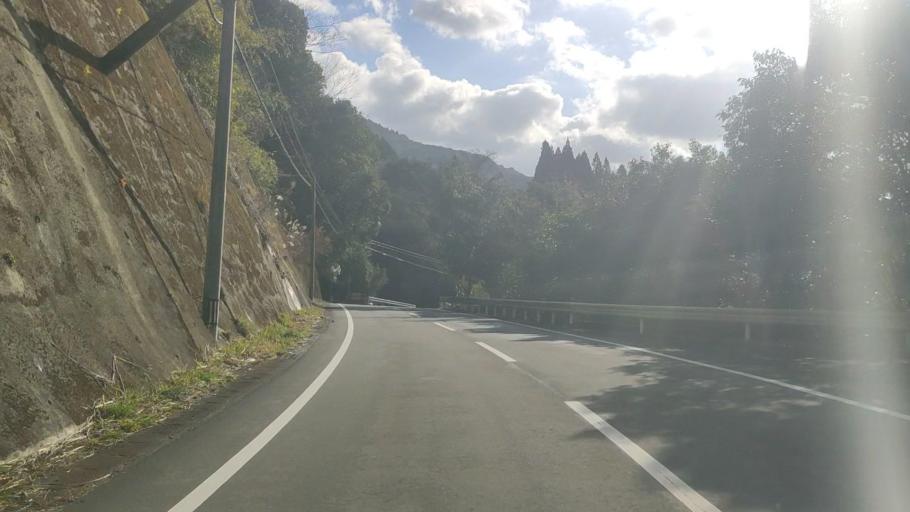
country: JP
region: Kumamoto
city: Hitoyoshi
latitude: 32.3190
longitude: 130.8426
